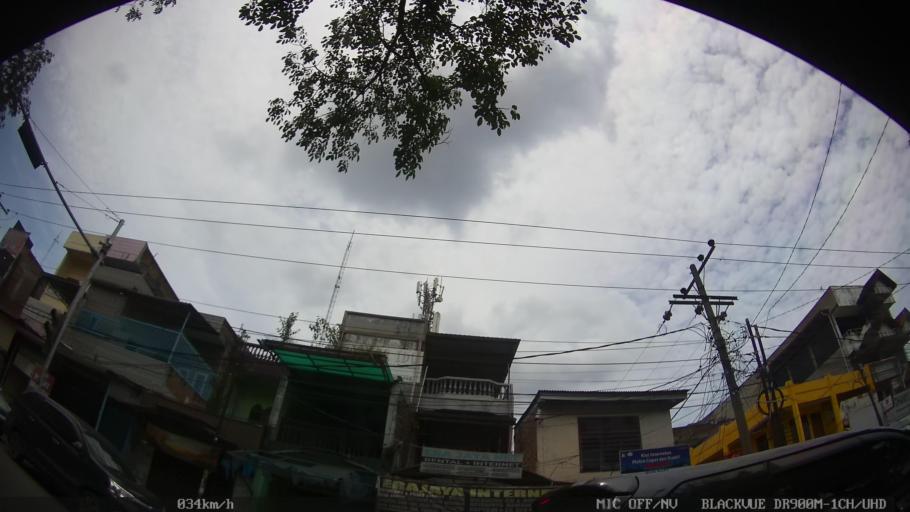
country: ID
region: North Sumatra
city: Medan
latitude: 3.5587
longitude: 98.6616
